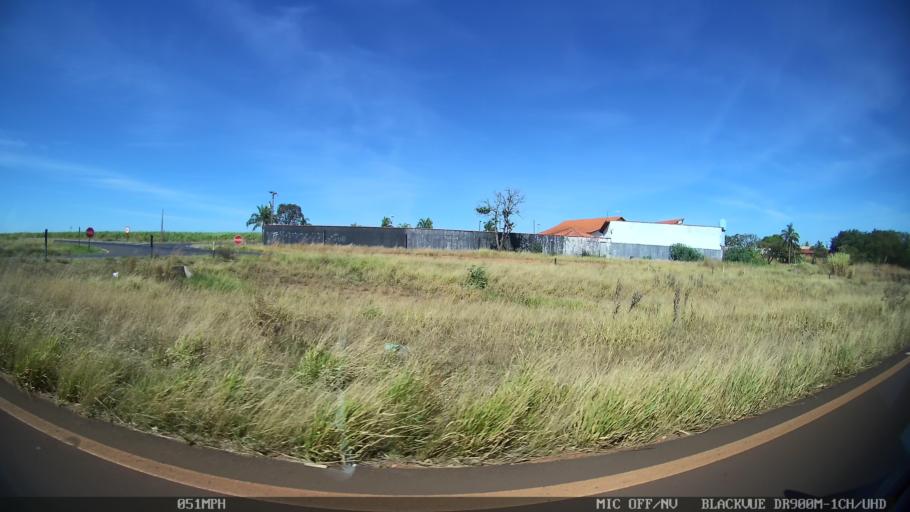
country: BR
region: Sao Paulo
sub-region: Franca
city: Franca
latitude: -20.5580
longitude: -47.5009
